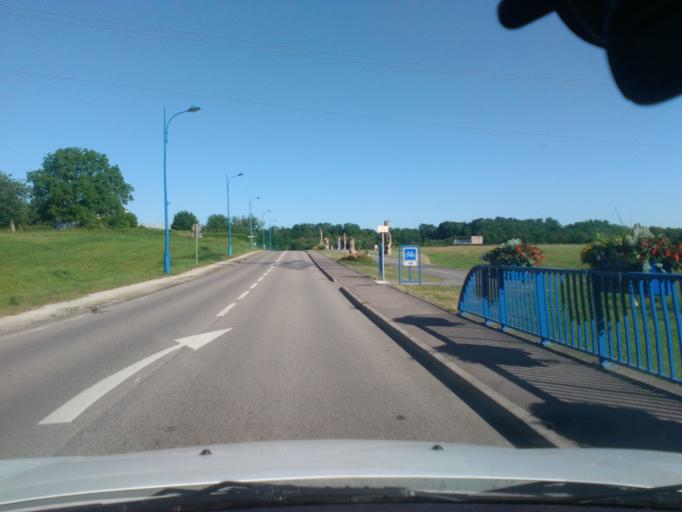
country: FR
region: Lorraine
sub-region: Departement des Vosges
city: Mirecourt
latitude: 48.2846
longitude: 6.1303
